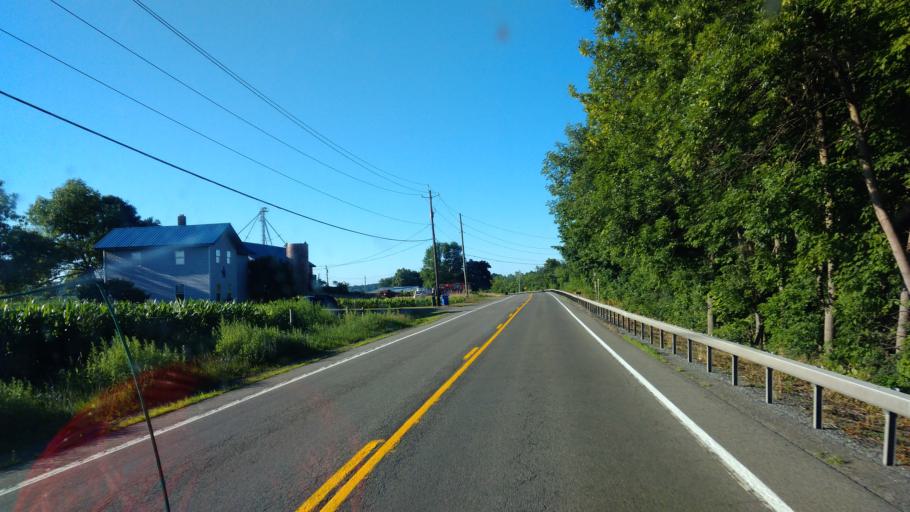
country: US
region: New York
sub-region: Wayne County
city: Lyons
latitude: 43.0414
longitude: -76.9934
